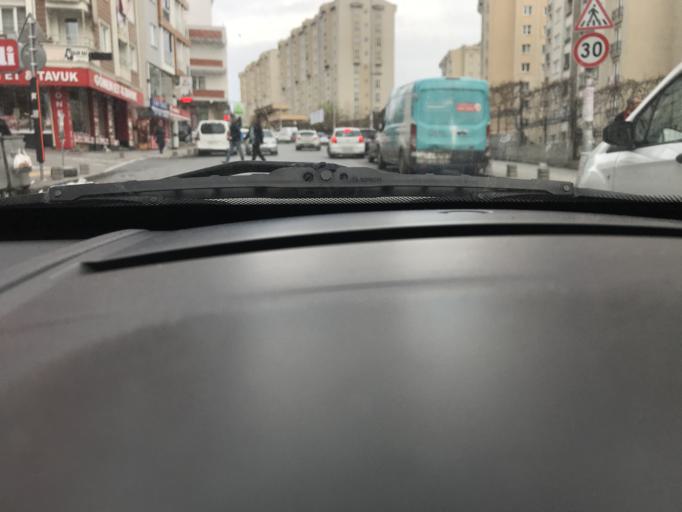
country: TR
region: Istanbul
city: Yakuplu
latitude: 41.0038
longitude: 28.6916
